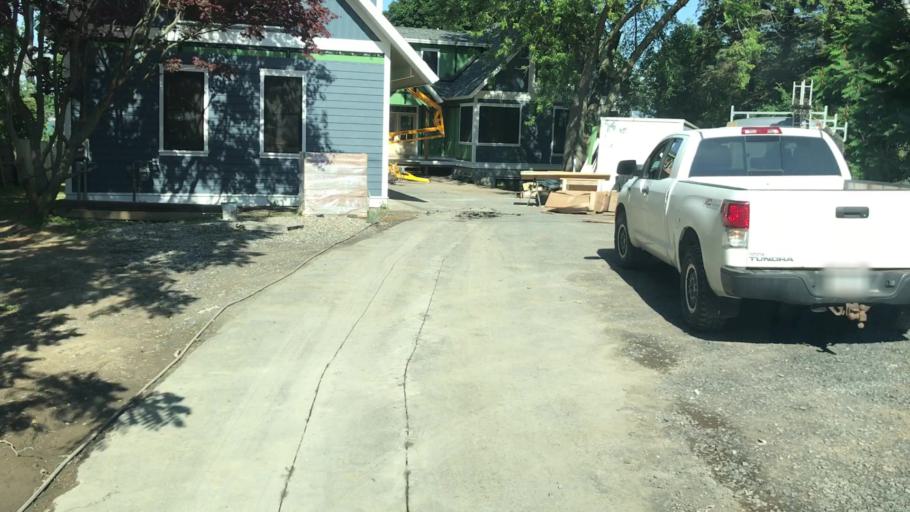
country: US
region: New York
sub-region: Onondaga County
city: Skaneateles
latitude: 42.9274
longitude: -76.4091
